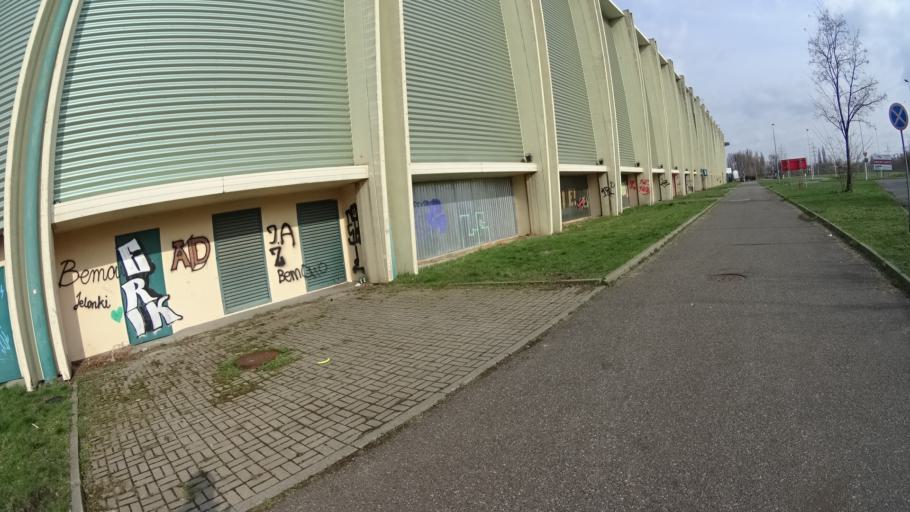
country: PL
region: Masovian Voivodeship
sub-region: Warszawa
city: Bemowo
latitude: 52.2240
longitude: 20.9245
